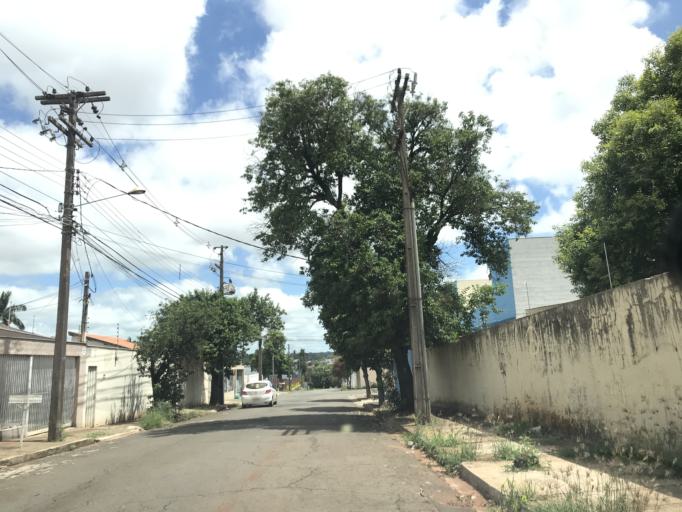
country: BR
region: Parana
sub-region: Londrina
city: Londrina
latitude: -23.2952
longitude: -51.1643
